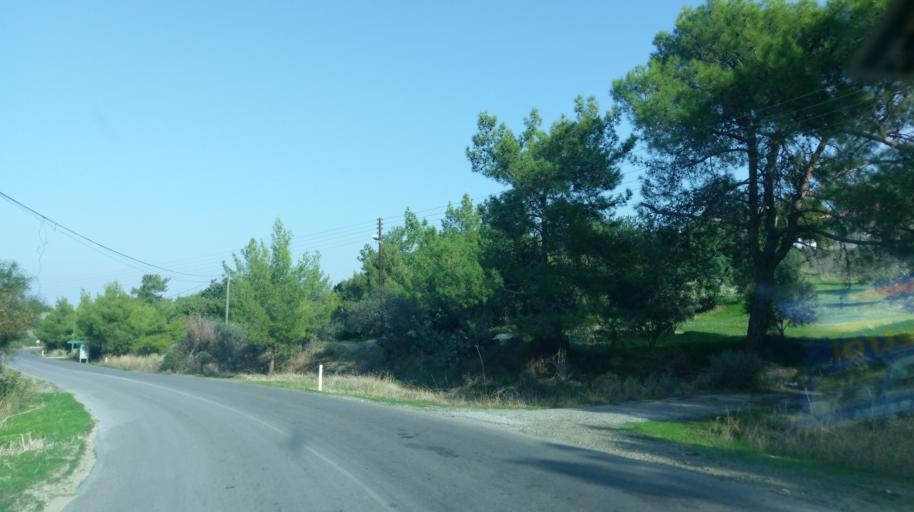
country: CY
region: Lefkosia
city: Kato Pyrgos
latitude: 35.1578
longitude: 32.7649
